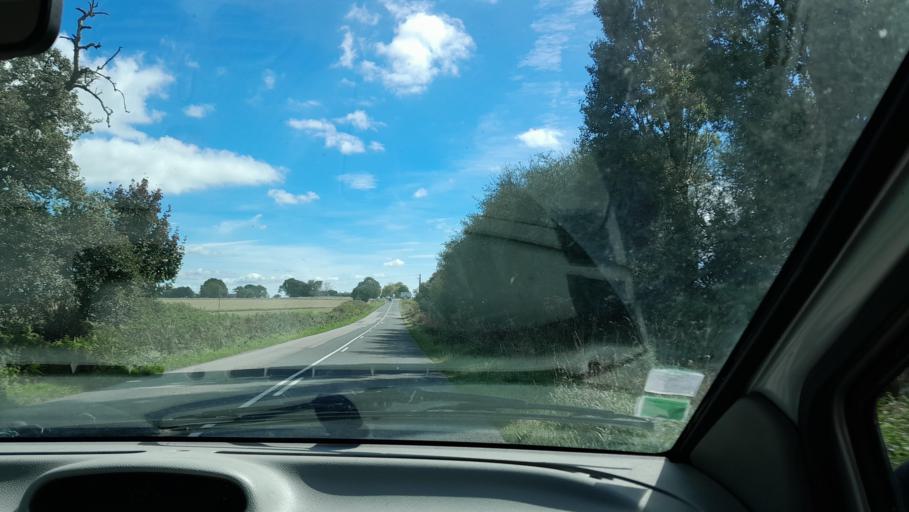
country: FR
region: Pays de la Loire
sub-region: Departement de la Mayenne
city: Cosse-le-Vivien
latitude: 47.9539
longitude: -0.9343
